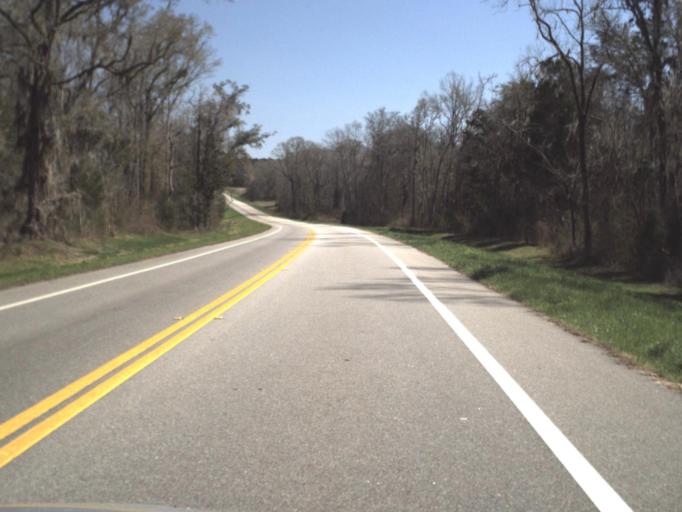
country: US
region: Florida
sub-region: Jackson County
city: Marianna
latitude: 30.8223
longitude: -85.3256
